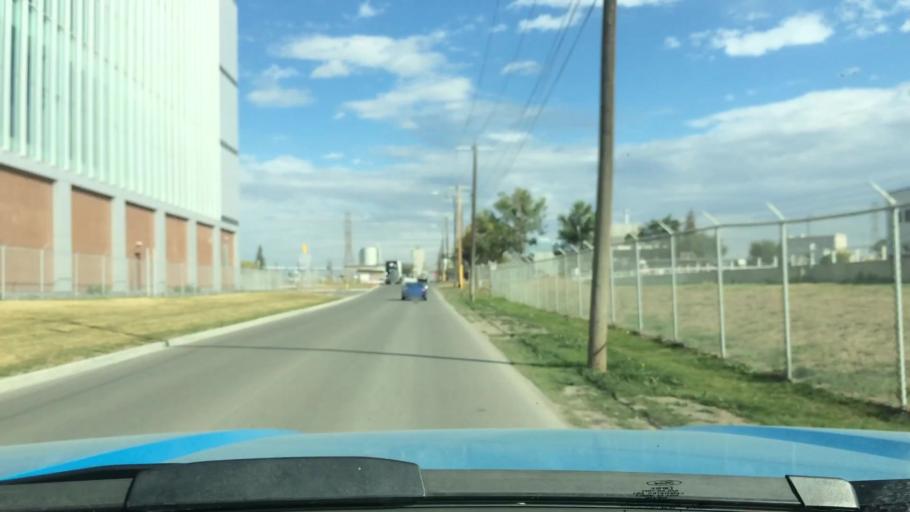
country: CA
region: Alberta
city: Calgary
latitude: 51.0116
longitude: -114.0251
